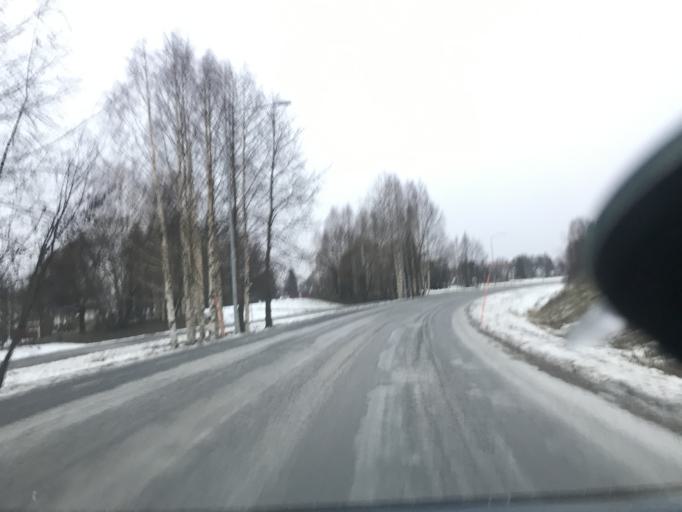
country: SE
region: Norrbotten
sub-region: Lulea Kommun
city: Sodra Sunderbyn
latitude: 65.6542
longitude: 21.9468
